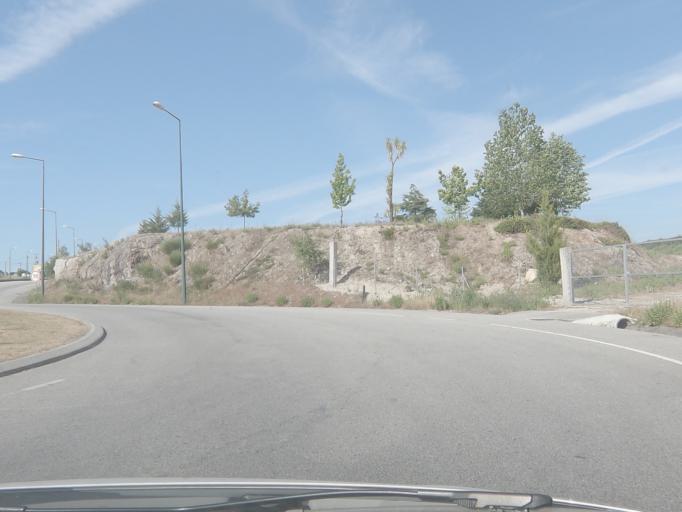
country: PT
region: Viseu
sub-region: Viseu
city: Viseu
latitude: 40.6247
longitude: -7.9433
